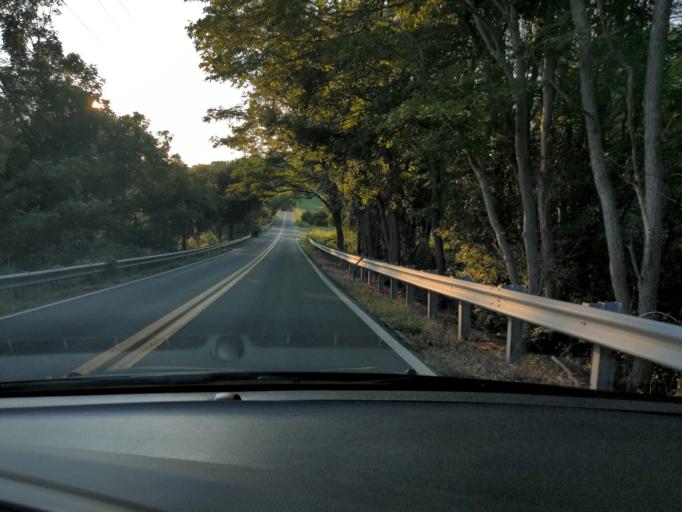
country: US
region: Maryland
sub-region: Carroll County
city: Hampstead
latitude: 39.5684
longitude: -76.8644
